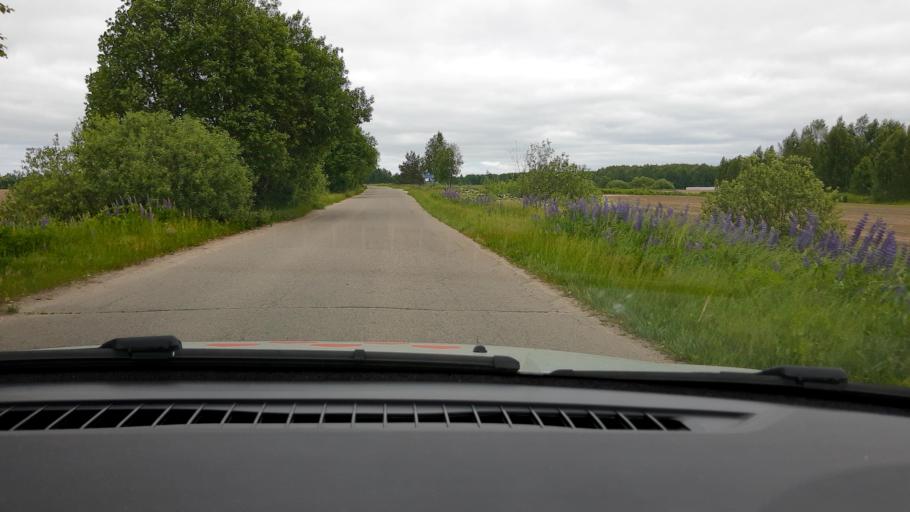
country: RU
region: Nizjnij Novgorod
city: Sitniki
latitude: 56.5086
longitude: 44.0971
